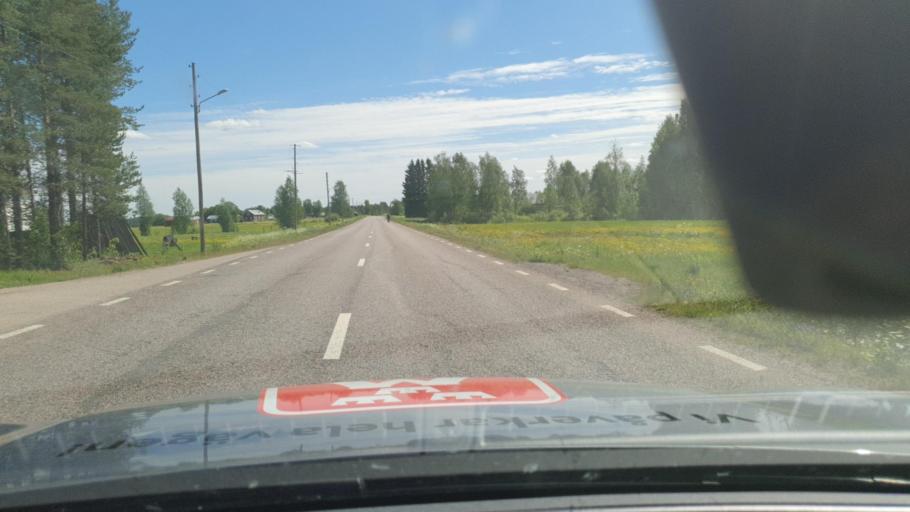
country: FI
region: Lapland
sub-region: Torniolaakso
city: Pello
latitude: 66.9872
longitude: 23.7868
